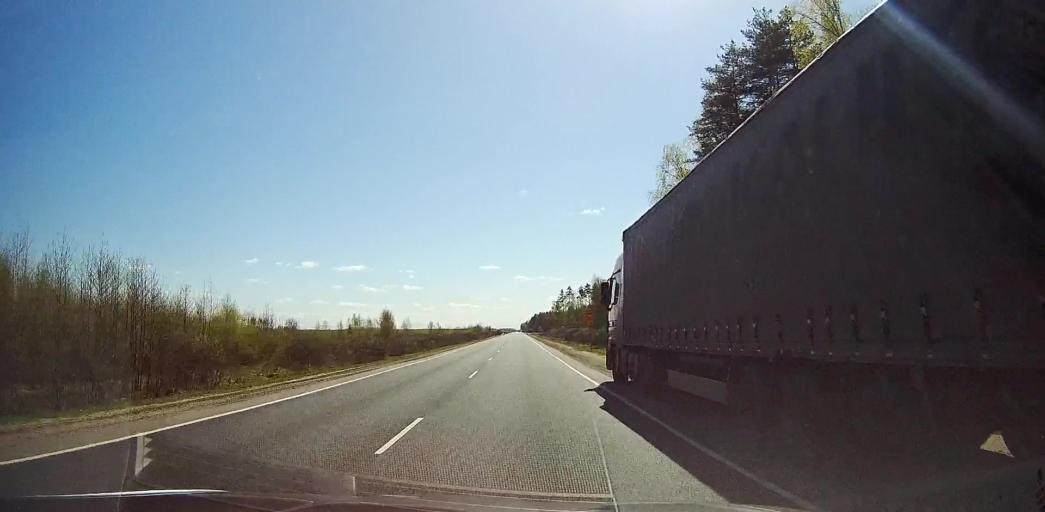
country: RU
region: Moskovskaya
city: Gzhel'
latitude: 55.5992
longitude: 38.3791
